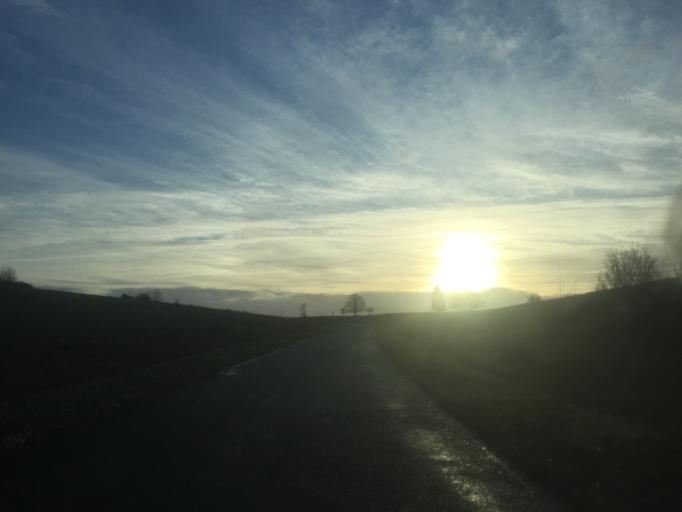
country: FR
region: Franche-Comte
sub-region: Departement du Jura
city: Dampierre
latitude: 47.1304
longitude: 5.7138
